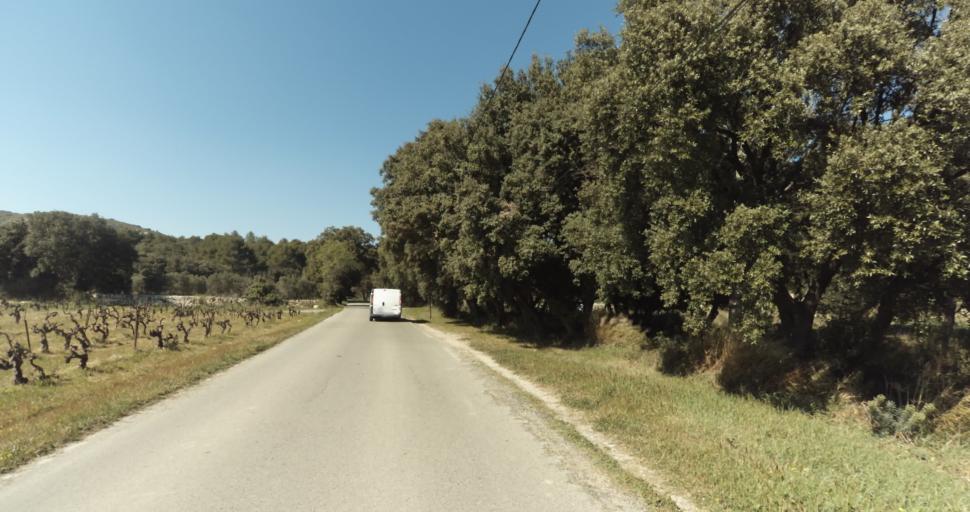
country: FR
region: Provence-Alpes-Cote d'Azur
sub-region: Departement des Bouches-du-Rhone
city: Pelissanne
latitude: 43.6476
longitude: 5.1817
